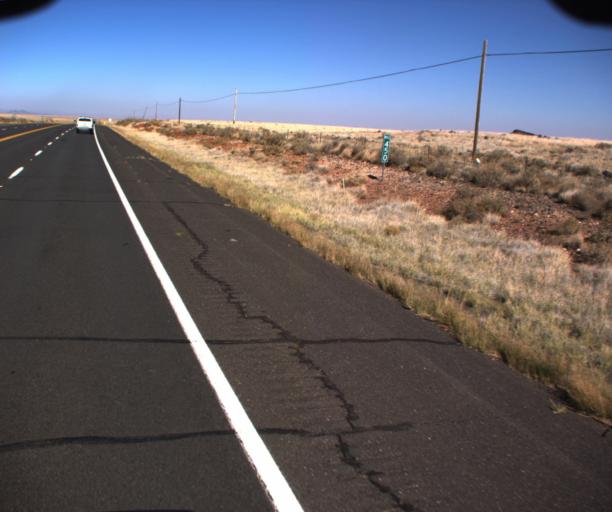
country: US
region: Arizona
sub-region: Coconino County
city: Flagstaff
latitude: 35.6491
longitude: -111.5163
